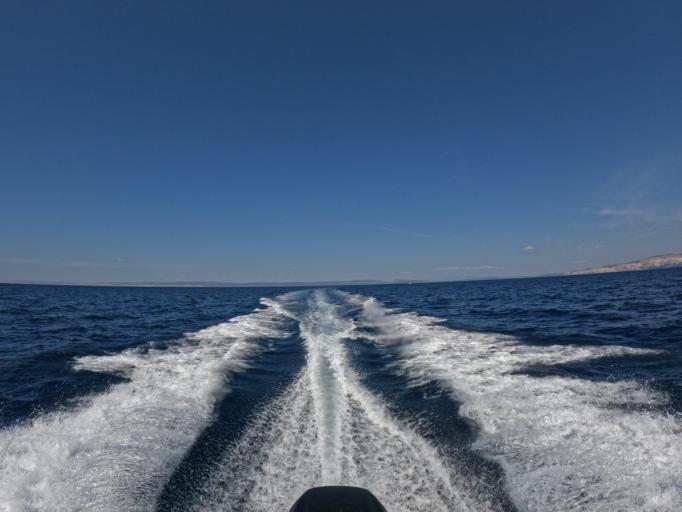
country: HR
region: Primorsko-Goranska
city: Lopar
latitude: 44.8635
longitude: 14.6845
